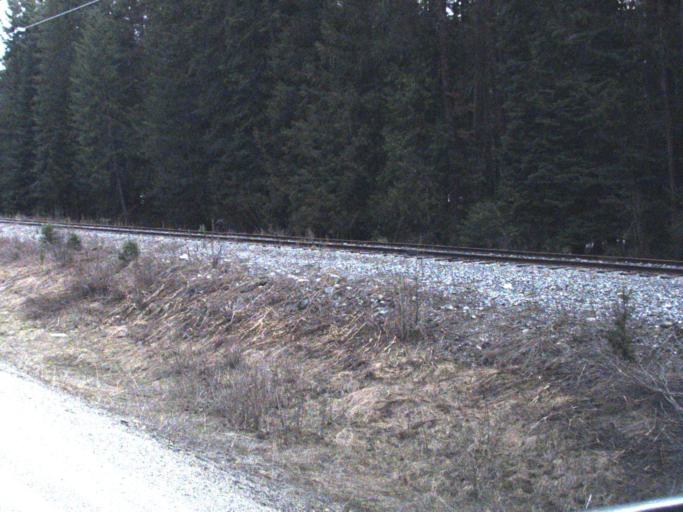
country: US
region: Washington
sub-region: Stevens County
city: Chewelah
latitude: 48.5768
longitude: -117.3522
